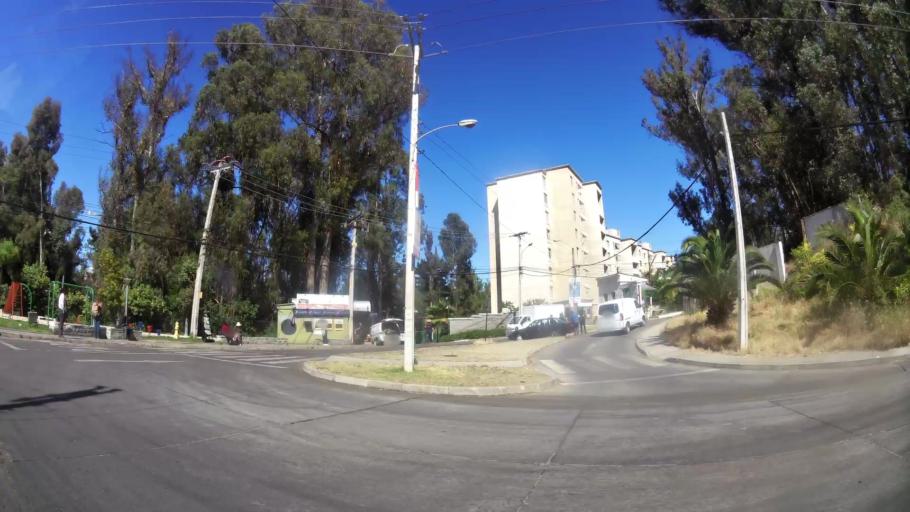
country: CL
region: Valparaiso
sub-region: Provincia de Valparaiso
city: Valparaiso
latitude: -33.0584
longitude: -71.5876
